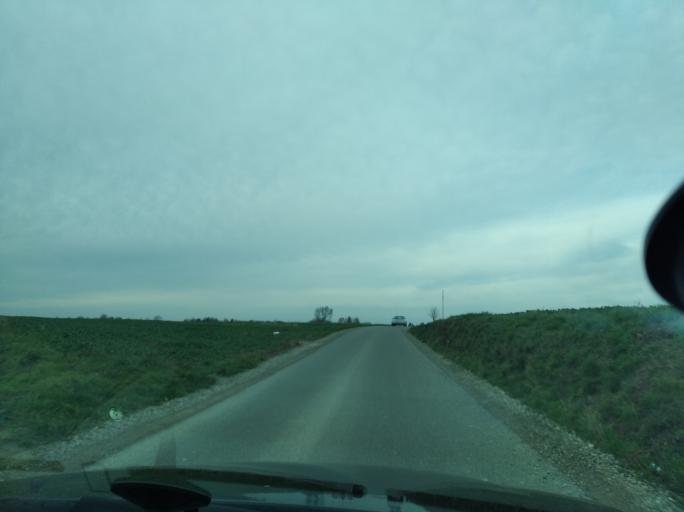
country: PL
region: Subcarpathian Voivodeship
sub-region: Powiat przeworski
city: Grzeska
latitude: 50.0682
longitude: 22.4620
